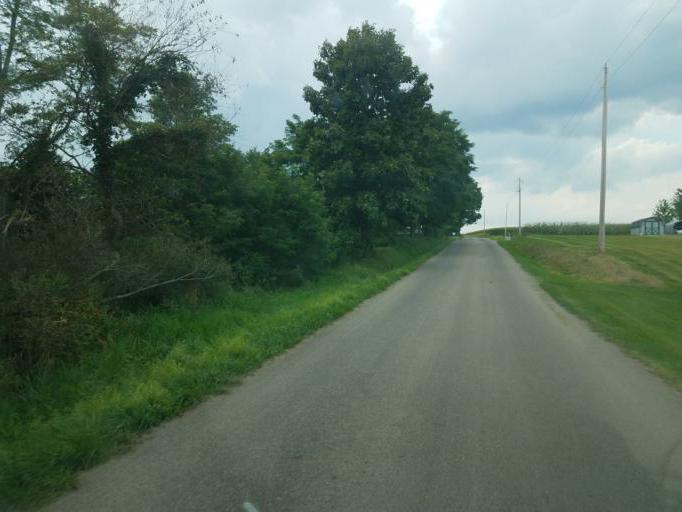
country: US
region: Ohio
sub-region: Knox County
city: Oak Hill
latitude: 40.3579
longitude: -82.3041
